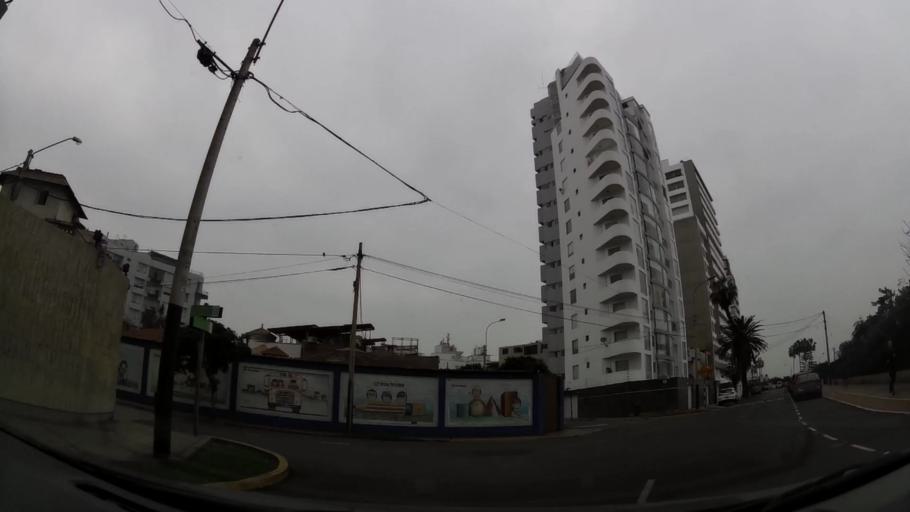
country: PE
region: Lima
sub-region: Lima
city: San Isidro
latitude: -12.1217
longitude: -77.0410
